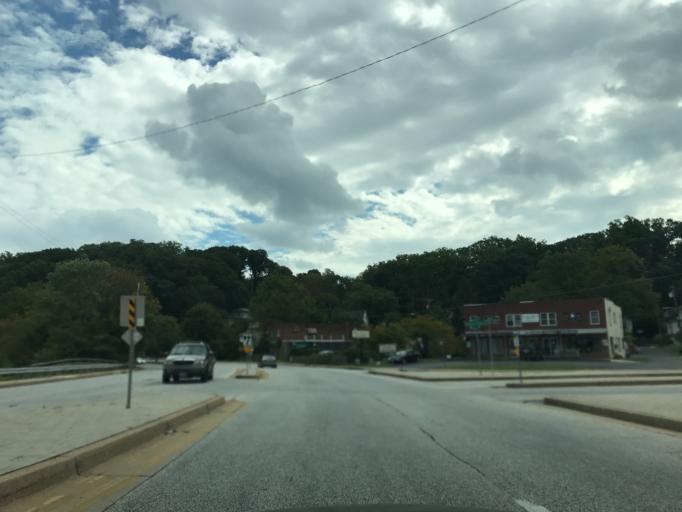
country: US
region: Maryland
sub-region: Baltimore County
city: Woodlawn
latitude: 39.3235
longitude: -76.7249
